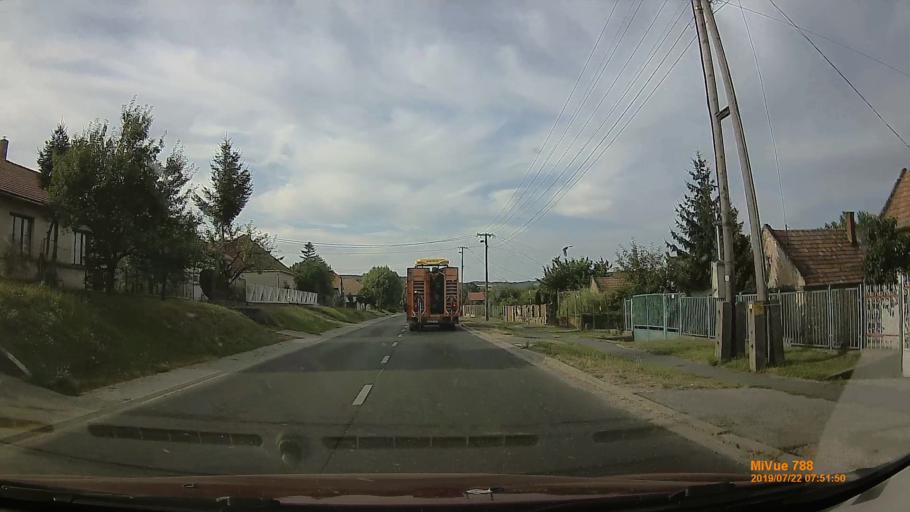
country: HU
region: Veszprem
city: Ajka
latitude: 47.0563
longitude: 17.5549
